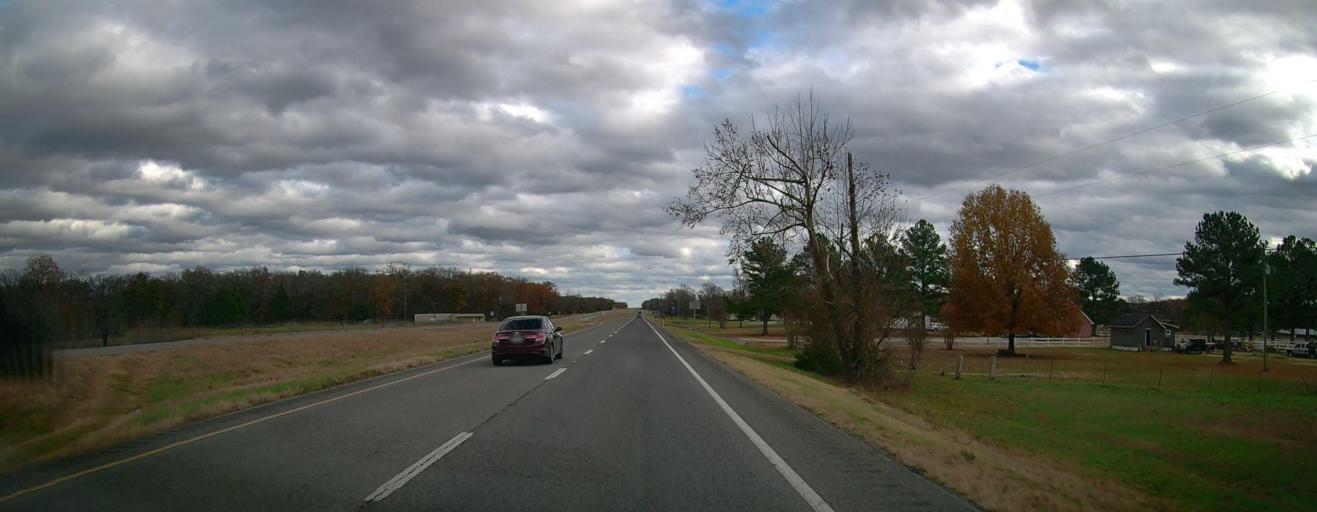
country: US
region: Alabama
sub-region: Morgan County
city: Danville
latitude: 34.4115
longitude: -87.1523
